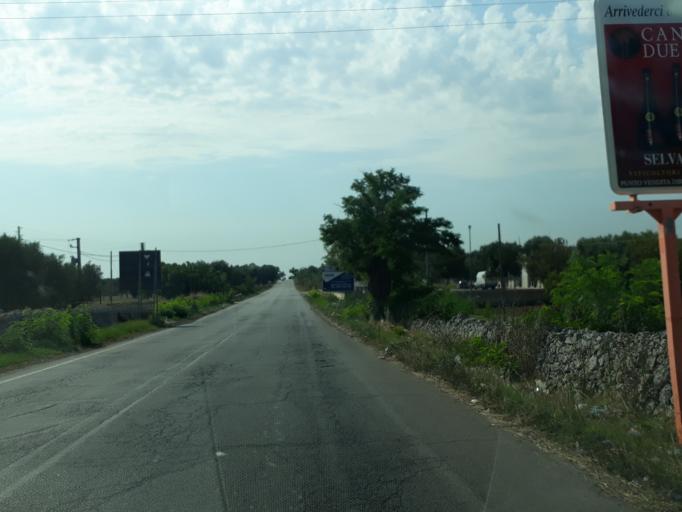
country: IT
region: Apulia
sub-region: Provincia di Brindisi
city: Carovigno
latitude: 40.6949
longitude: 17.6694
